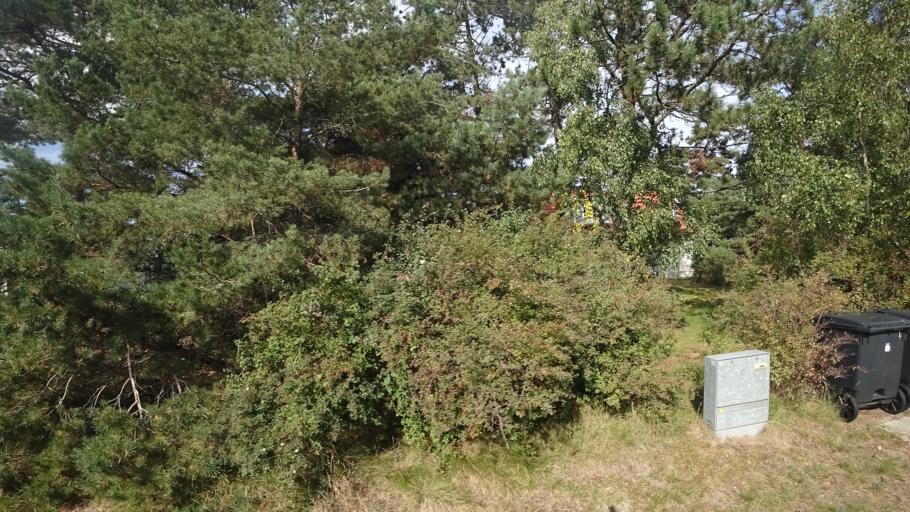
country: SE
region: Skane
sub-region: Kristianstads Kommun
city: Ahus
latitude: 55.9107
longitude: 14.2871
